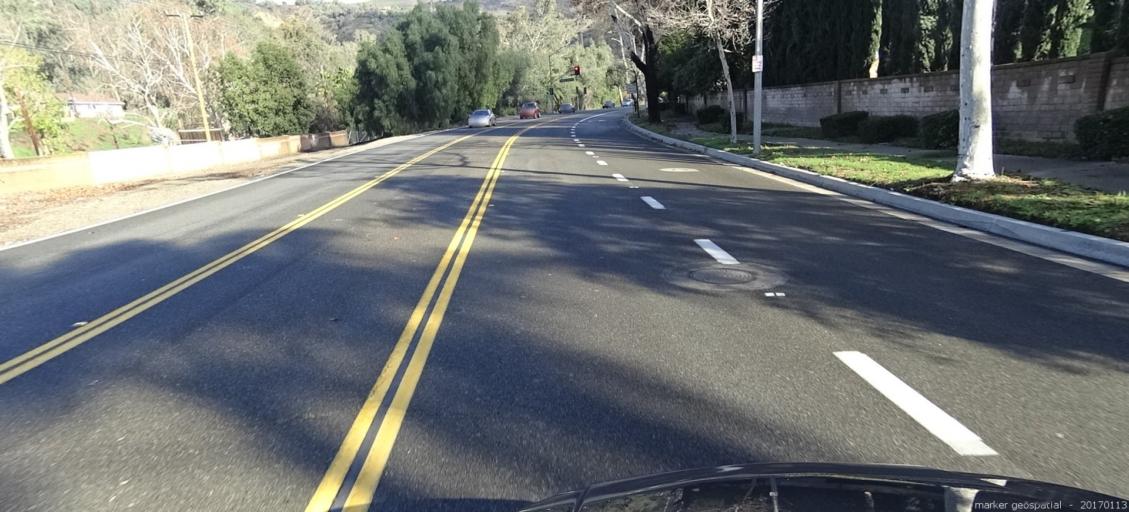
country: US
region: California
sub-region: Orange County
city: Brea
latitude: 33.9351
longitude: -117.8932
